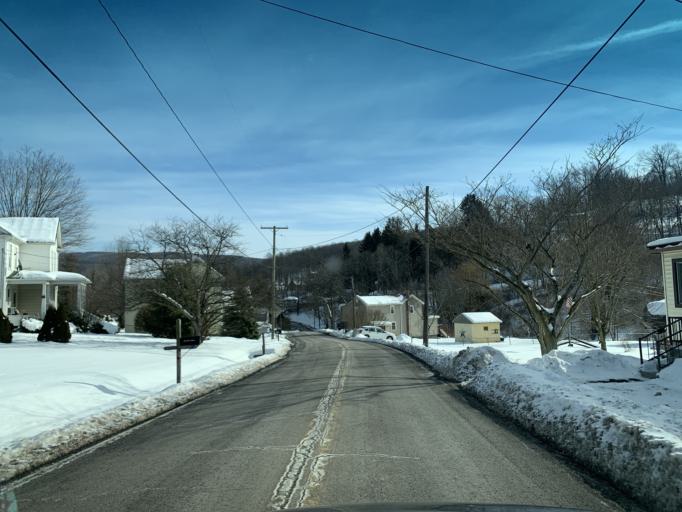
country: US
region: Maryland
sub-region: Allegany County
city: Frostburg
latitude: 39.6521
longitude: -78.8968
